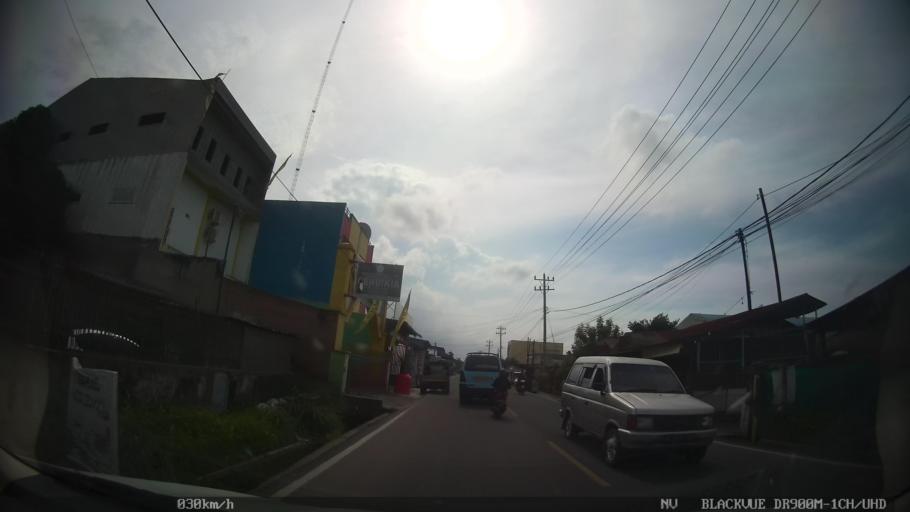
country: ID
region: North Sumatra
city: Percut
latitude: 3.6072
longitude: 98.7664
